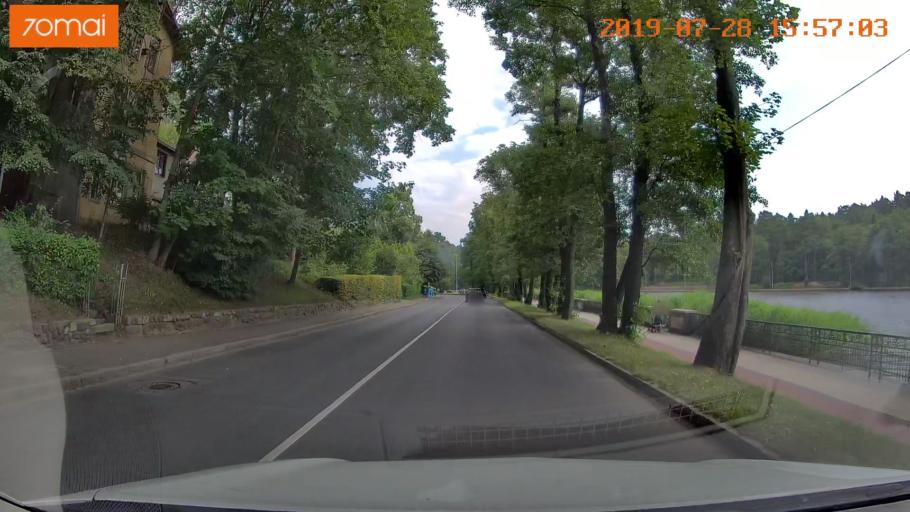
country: RU
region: Kaliningrad
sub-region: Gorod Svetlogorsk
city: Svetlogorsk
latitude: 54.9390
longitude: 20.1516
